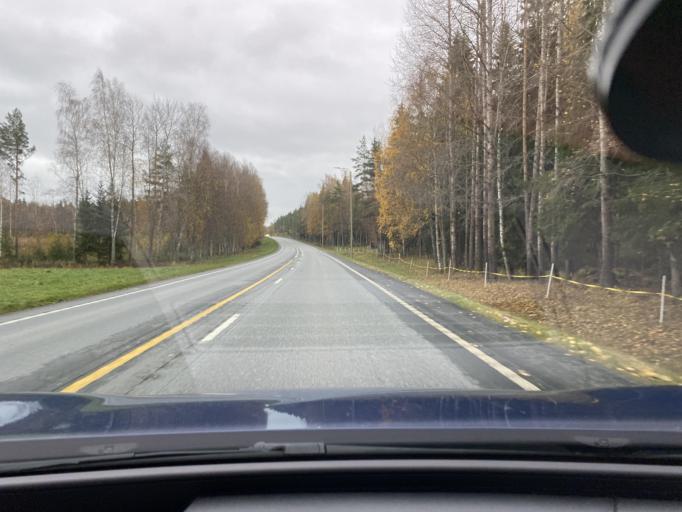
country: FI
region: Varsinais-Suomi
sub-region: Vakka-Suomi
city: Laitila
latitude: 60.9343
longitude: 21.6056
